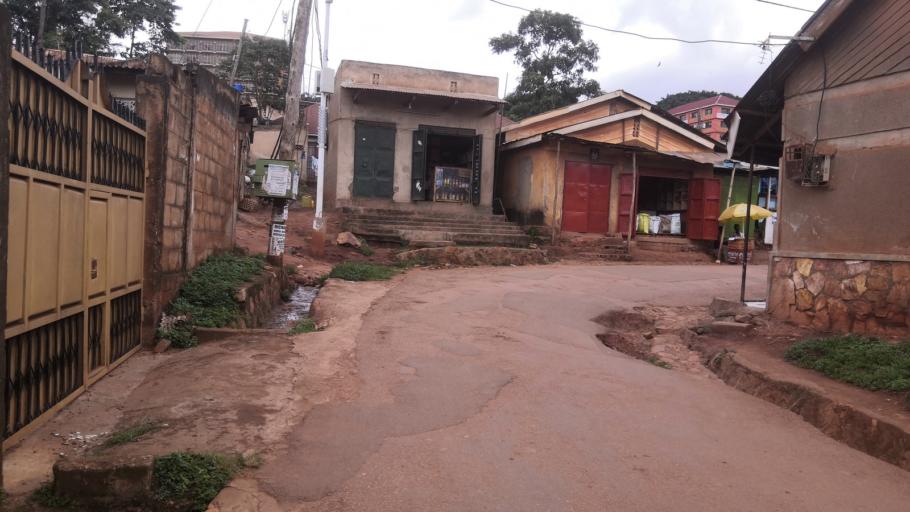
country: UG
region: Central Region
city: Kampala Central Division
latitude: 0.3296
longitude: 32.5629
